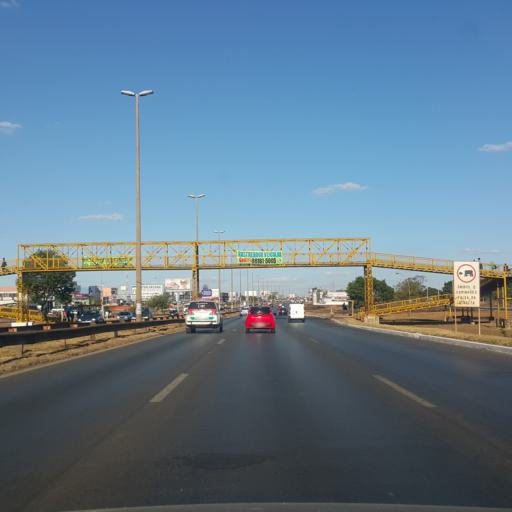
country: BR
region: Federal District
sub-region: Brasilia
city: Brasilia
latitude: -15.7899
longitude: -47.9817
